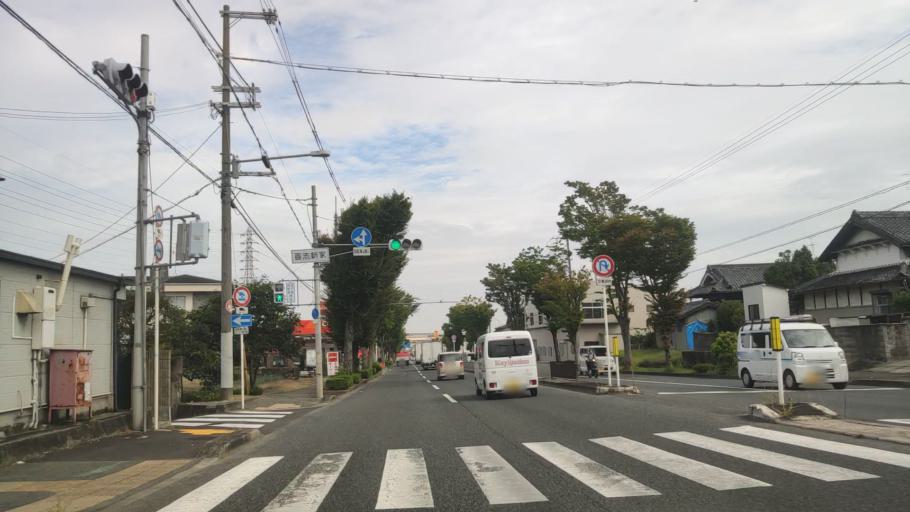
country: JP
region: Osaka
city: Tondabayashicho
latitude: 34.5279
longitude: 135.6049
